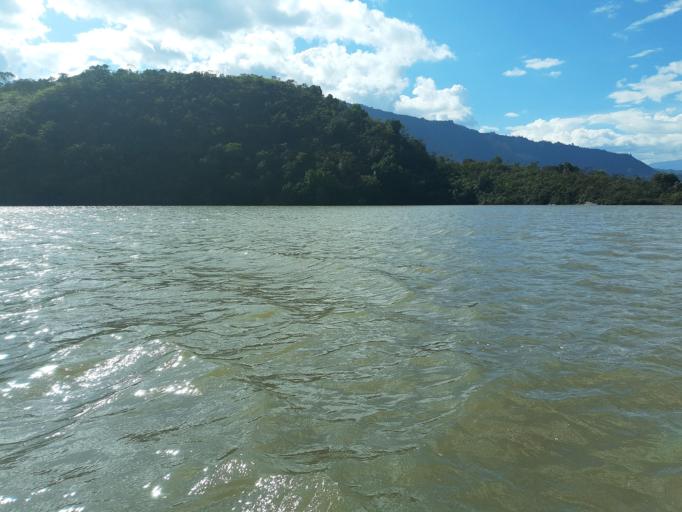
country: CO
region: Boyaca
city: Chivor
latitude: 4.9434
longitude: -73.3169
